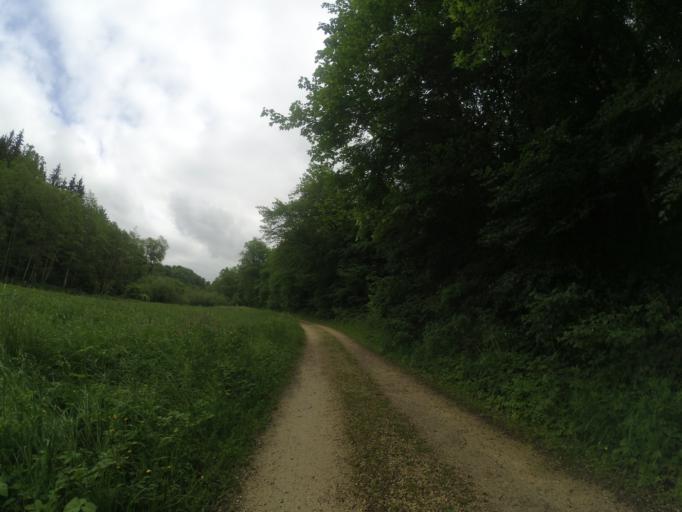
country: DE
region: Baden-Wuerttemberg
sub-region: Tuebingen Region
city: Bernstadt
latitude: 48.5176
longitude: 10.0422
